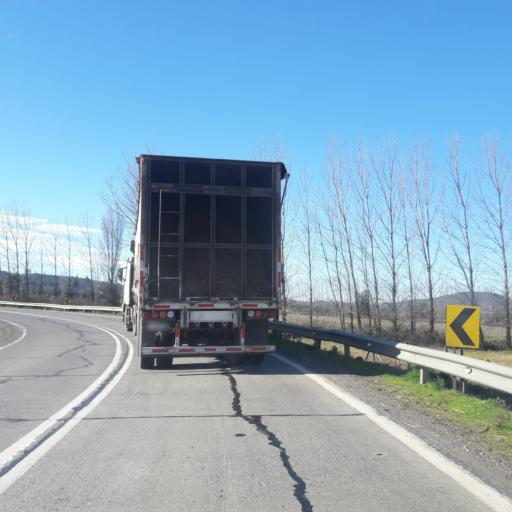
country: CL
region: Araucania
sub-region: Provincia de Malleco
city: Angol
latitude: -37.7849
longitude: -72.5268
